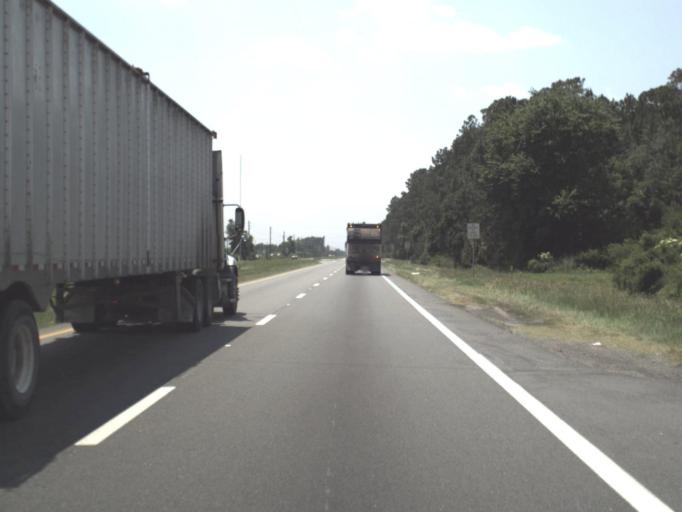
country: US
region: Florida
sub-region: Duval County
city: Baldwin
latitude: 30.2826
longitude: -81.9837
